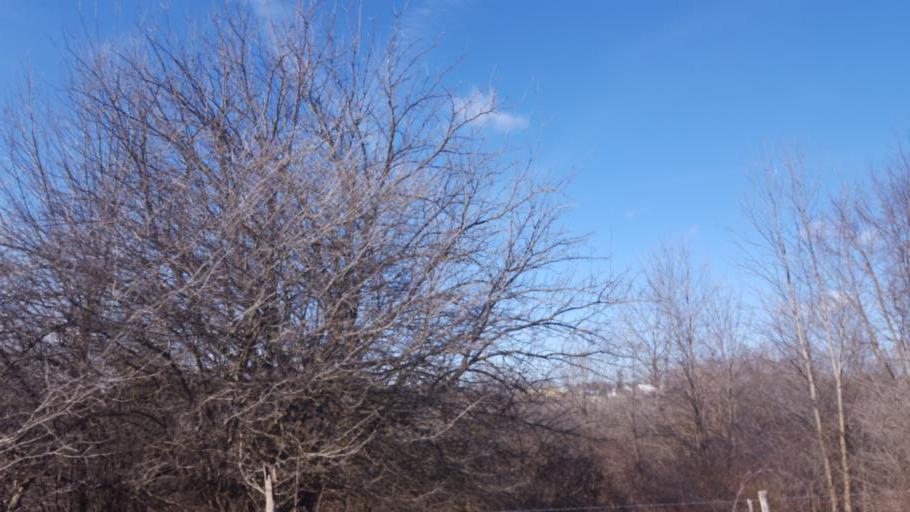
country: US
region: Ohio
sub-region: Knox County
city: Fredericktown
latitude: 40.5434
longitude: -82.5951
